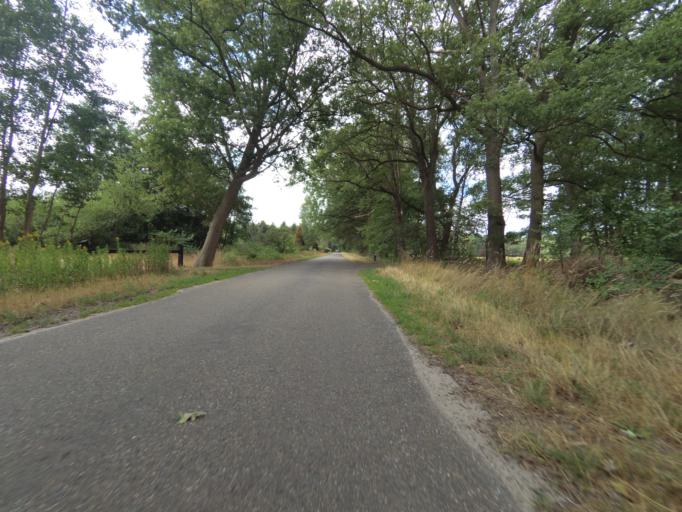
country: NL
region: Overijssel
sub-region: Gemeente Hof van Twente
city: Delden
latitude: 52.2870
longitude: 6.6824
